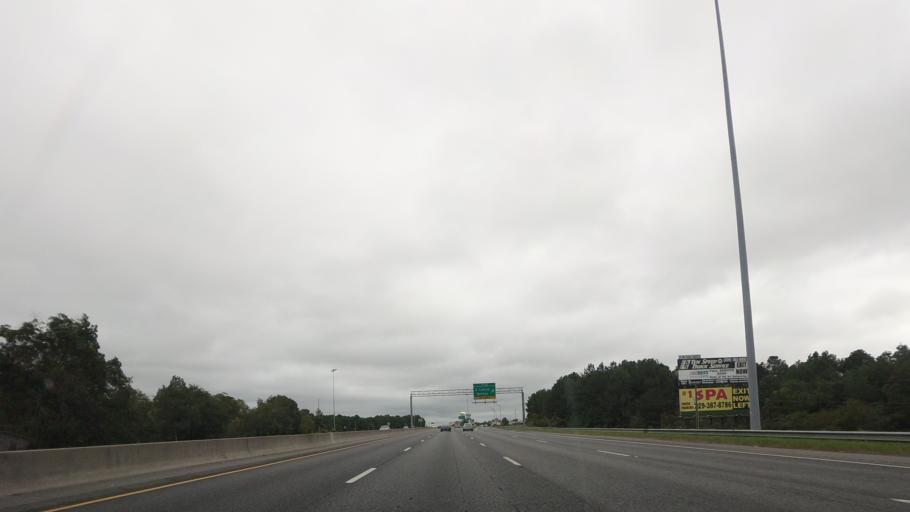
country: US
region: Georgia
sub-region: Tift County
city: Unionville
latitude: 31.4338
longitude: -83.5201
